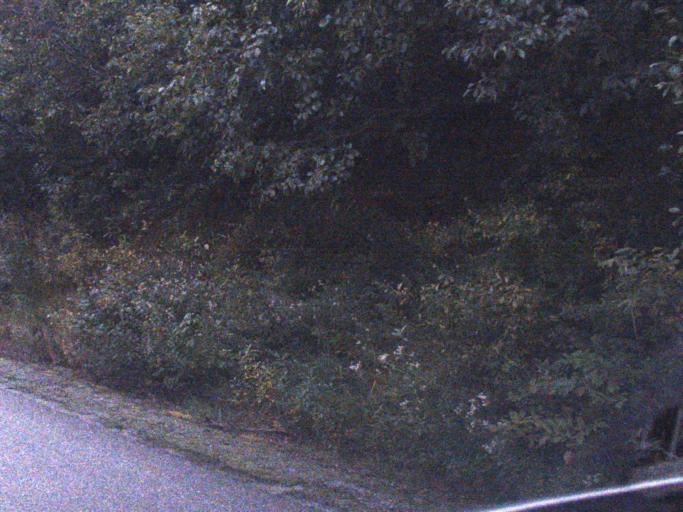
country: US
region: Washington
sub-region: Snohomish County
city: Darrington
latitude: 48.6405
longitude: -120.8519
